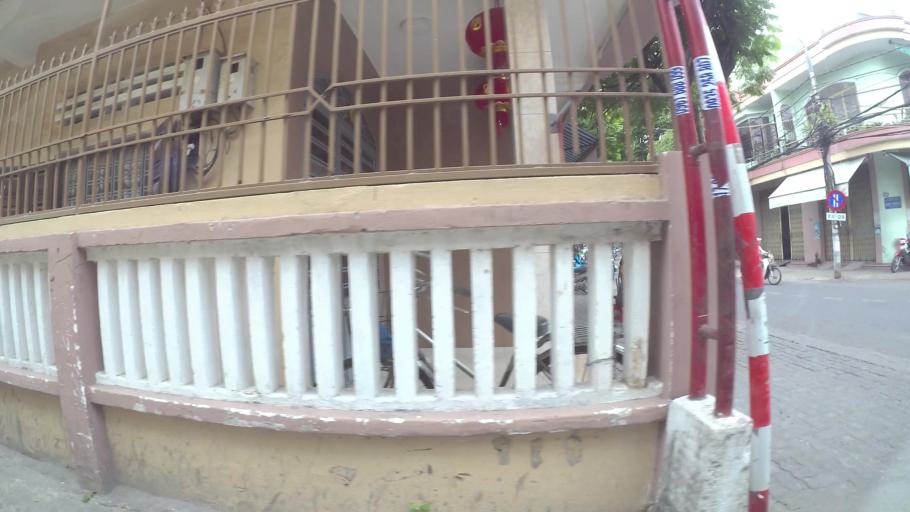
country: VN
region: Da Nang
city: Thanh Khe
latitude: 16.0681
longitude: 108.1986
